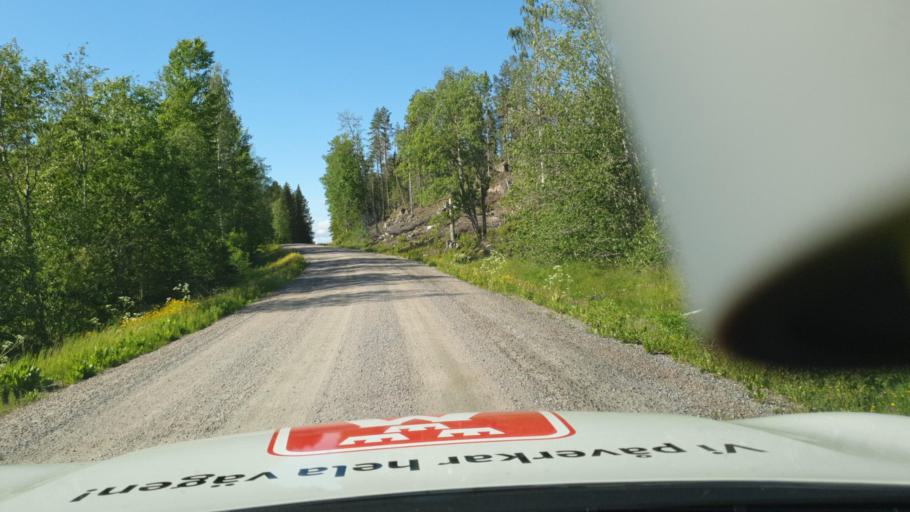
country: SE
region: Vaesterbotten
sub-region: Vannas Kommun
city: Vaennaes
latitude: 63.8366
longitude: 19.6315
